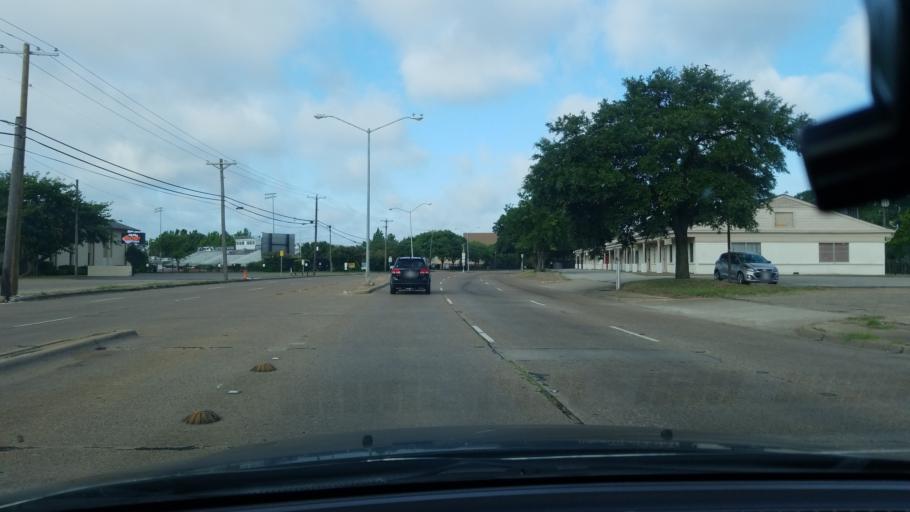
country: US
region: Texas
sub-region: Dallas County
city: Mesquite
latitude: 32.8209
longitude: -96.6791
